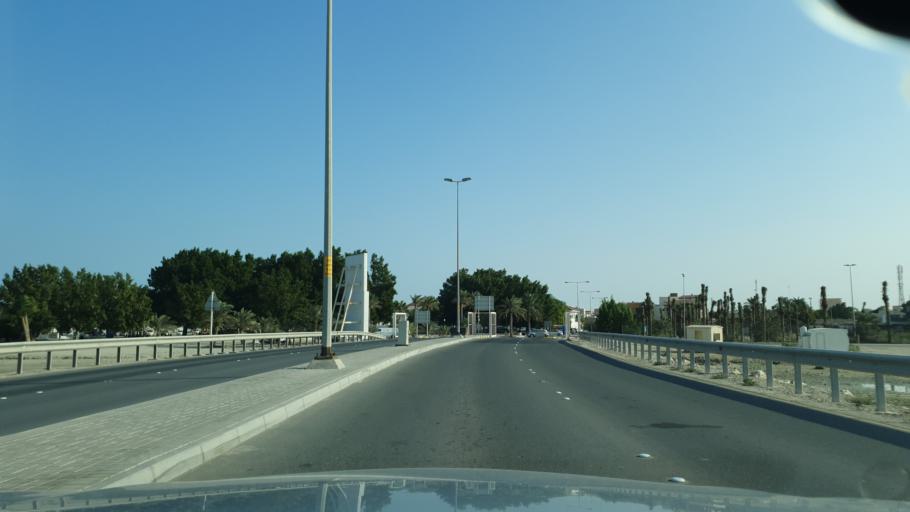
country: BH
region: Manama
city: Jidd Hafs
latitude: 26.2250
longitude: 50.4589
